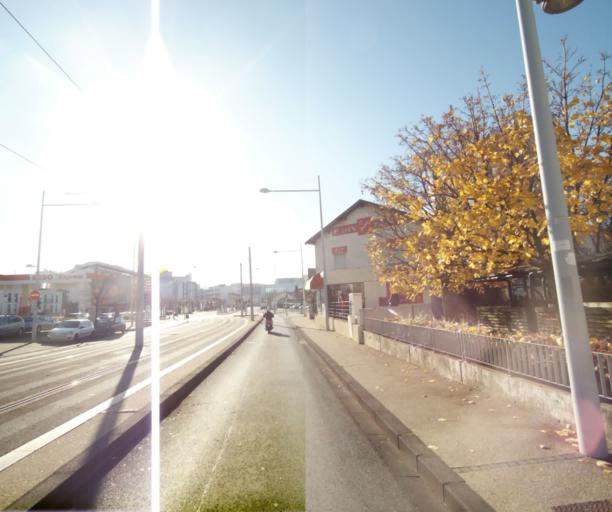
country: FR
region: Auvergne
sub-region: Departement du Puy-de-Dome
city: Beaumont
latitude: 45.7627
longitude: 3.0891
